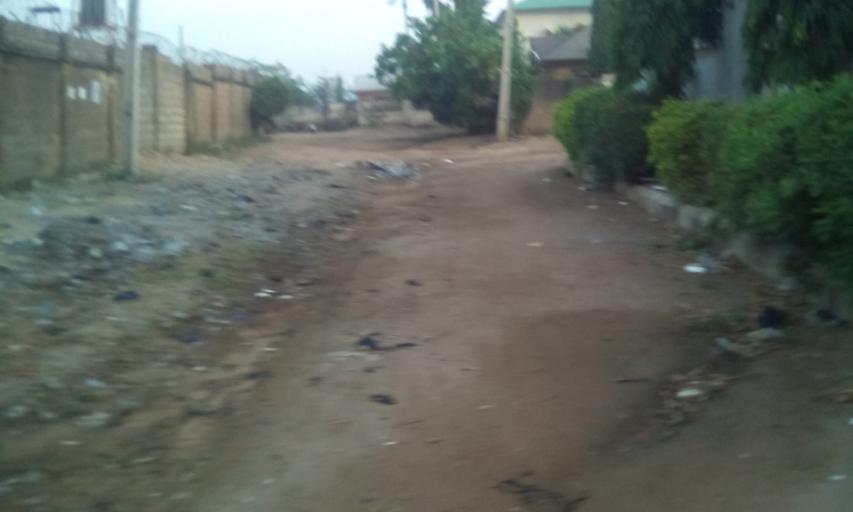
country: NG
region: Abuja Federal Capital Territory
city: Abuja
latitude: 8.9901
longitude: 7.3548
